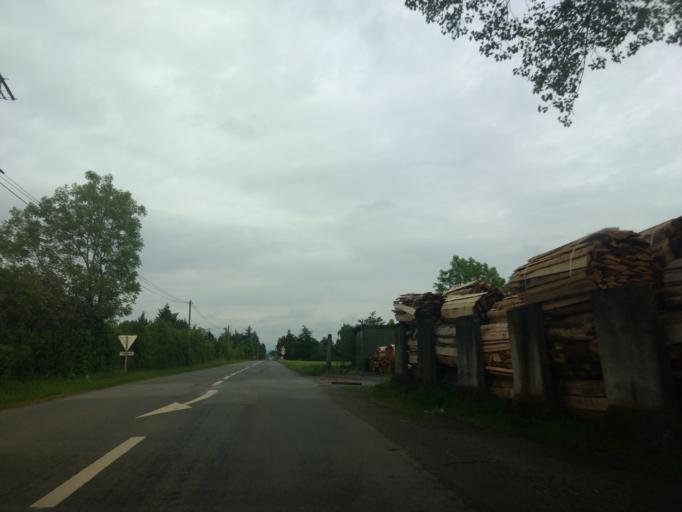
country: FR
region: Midi-Pyrenees
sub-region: Departement de l'Aveyron
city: Montbazens
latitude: 44.4606
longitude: 2.2240
